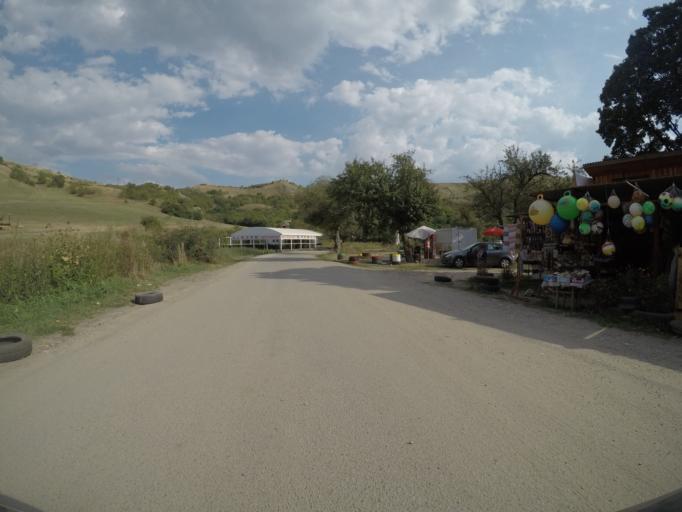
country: RO
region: Cluj
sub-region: Comuna Sandulesti
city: Sandulesti
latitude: 46.5615
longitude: 23.6912
